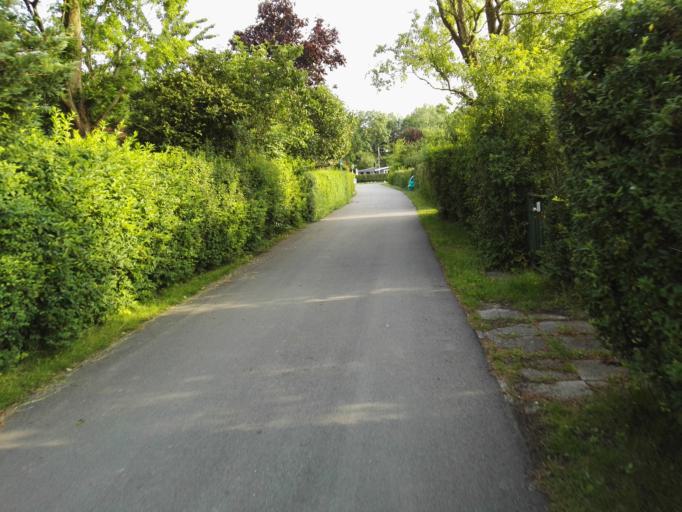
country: DK
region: Capital Region
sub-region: Ballerup Kommune
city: Ballerup
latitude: 55.7214
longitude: 12.3407
